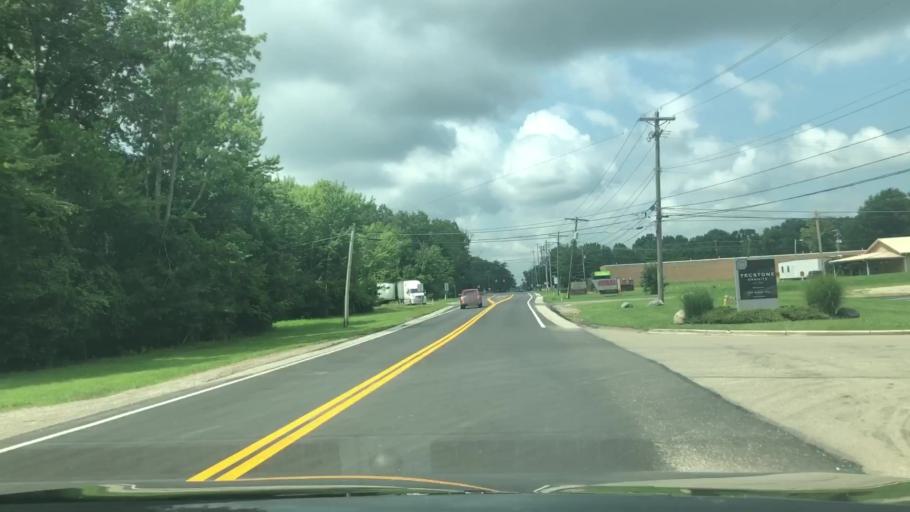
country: US
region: Ohio
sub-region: Franklin County
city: Gahanna
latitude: 40.0201
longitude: -82.9067
